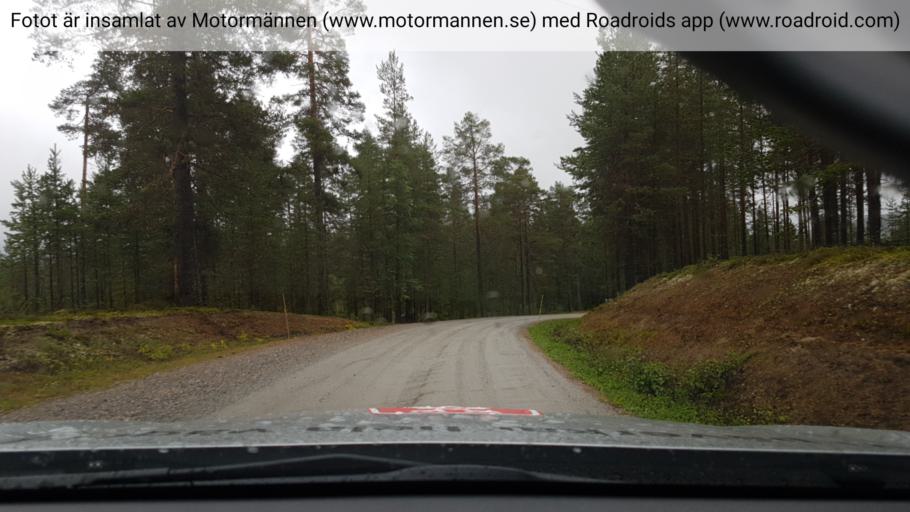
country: SE
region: Vaesterbotten
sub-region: Asele Kommun
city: Asele
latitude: 64.0246
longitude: 17.6628
